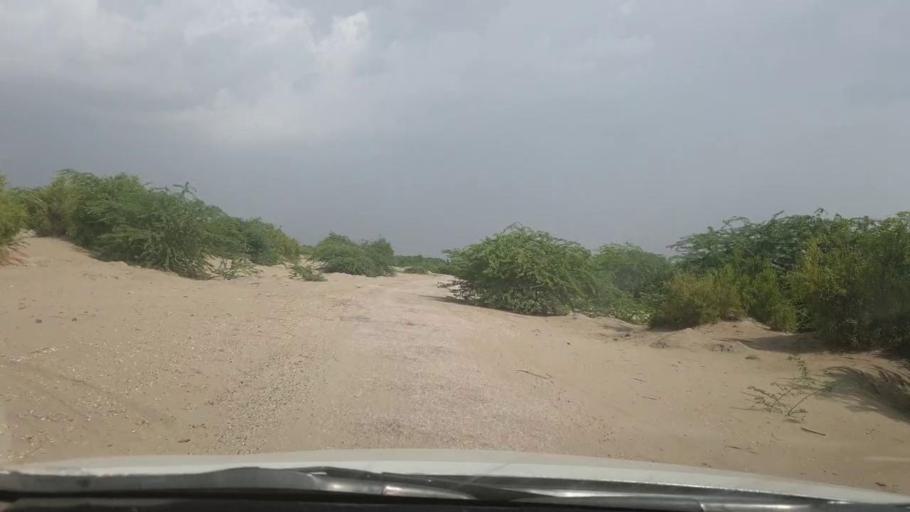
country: PK
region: Sindh
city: Kot Diji
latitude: 27.3345
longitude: 69.0474
